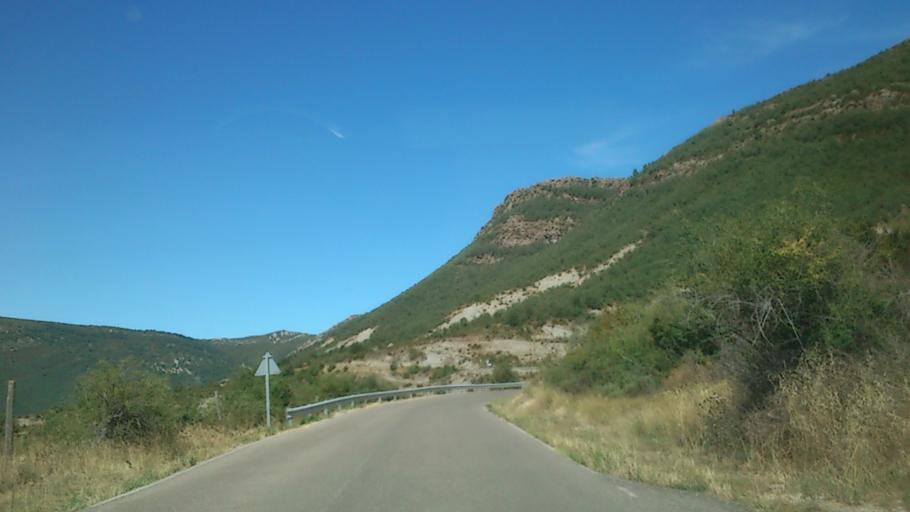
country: ES
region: Aragon
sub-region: Provincia de Huesca
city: Arguis
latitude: 42.3159
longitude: -0.4399
